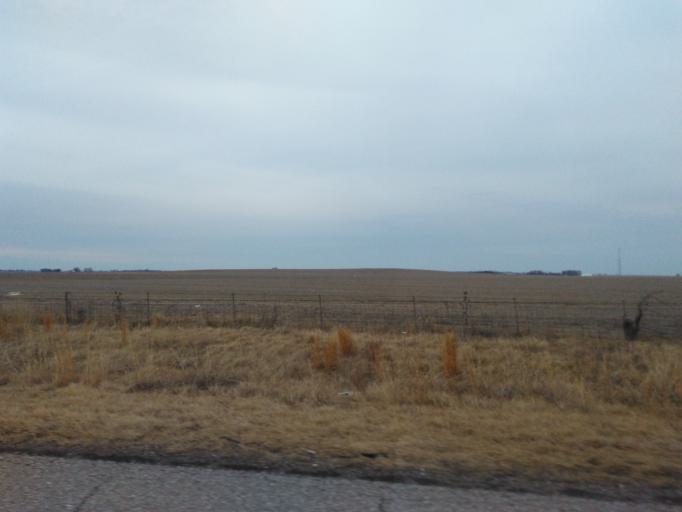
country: US
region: Illinois
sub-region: Washington County
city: Nashville
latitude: 38.3913
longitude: -89.2805
